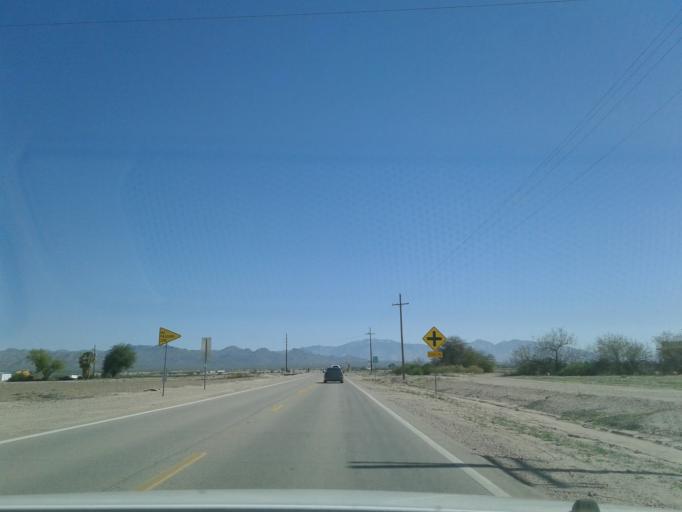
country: US
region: Arizona
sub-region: Pima County
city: Marana
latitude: 32.4605
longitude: -111.2364
